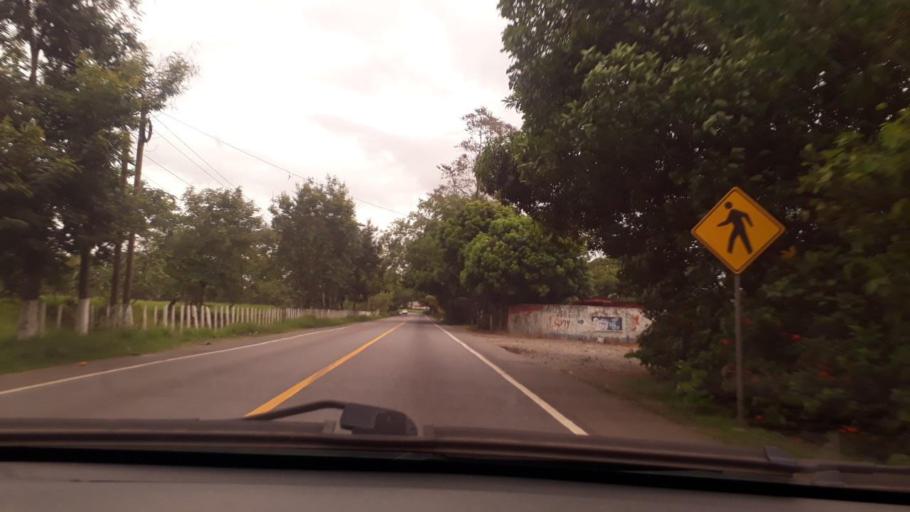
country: GT
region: Izabal
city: Morales
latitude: 15.4817
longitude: -88.8751
